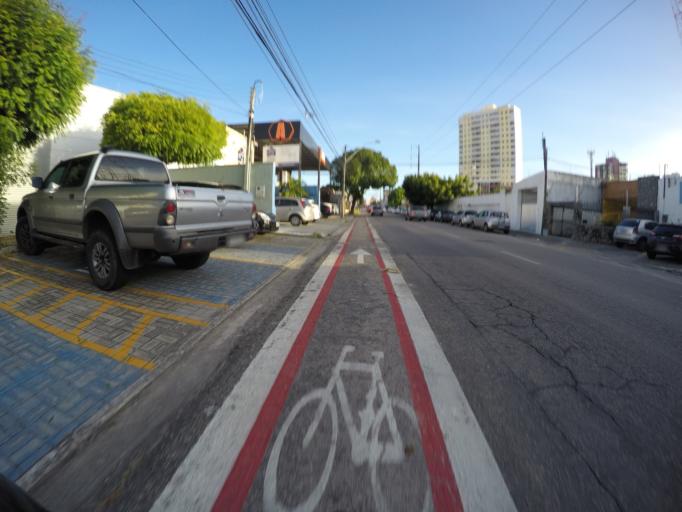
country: BR
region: Ceara
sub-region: Fortaleza
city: Fortaleza
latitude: -3.7475
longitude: -38.5131
